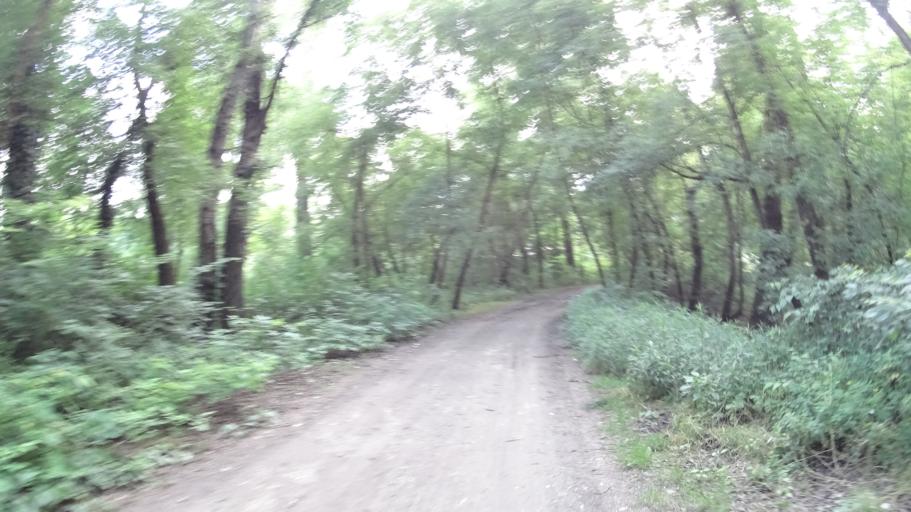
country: HU
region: Pest
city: Szodliget
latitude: 47.7333
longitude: 19.1364
